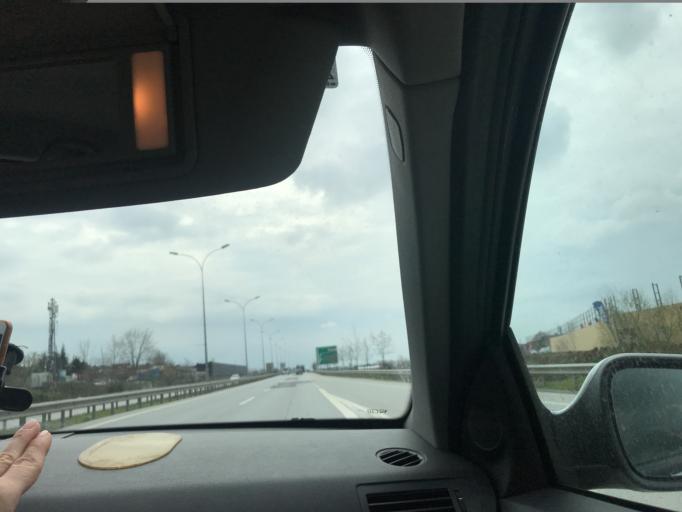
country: TR
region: Istanbul
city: Sultanbeyli
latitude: 40.9285
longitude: 29.3268
